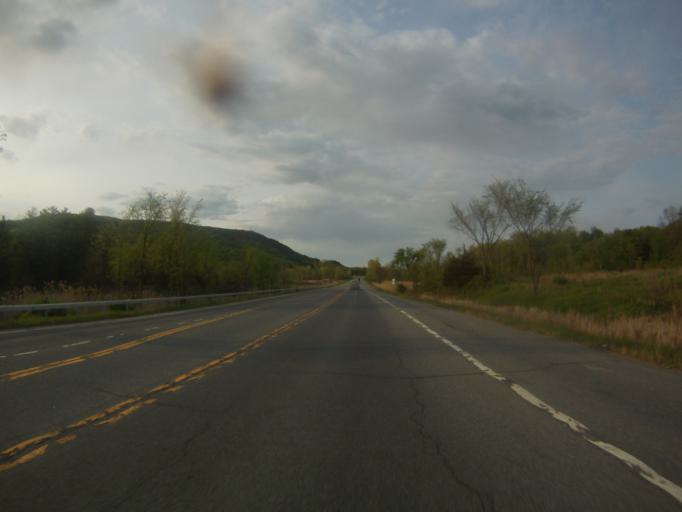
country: US
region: New York
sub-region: Essex County
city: Ticonderoga
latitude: 43.9019
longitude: -73.4266
